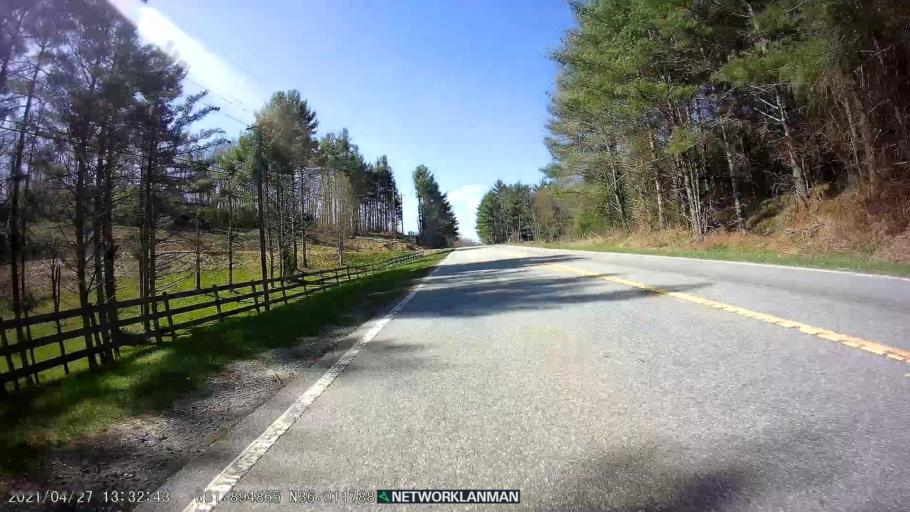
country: US
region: North Carolina
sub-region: Avery County
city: Newland
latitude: 36.0115
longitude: -81.8947
